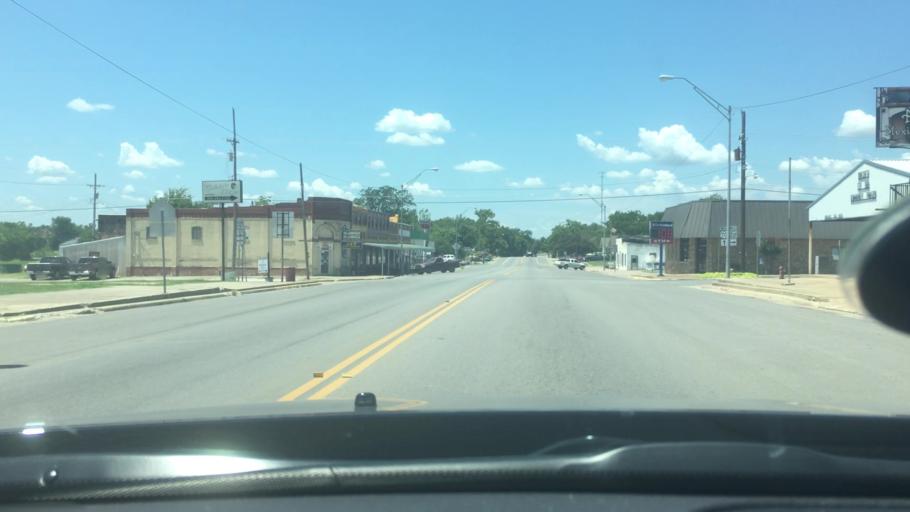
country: US
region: Oklahoma
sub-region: Bryan County
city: Durant
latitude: 34.0167
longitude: -96.1439
